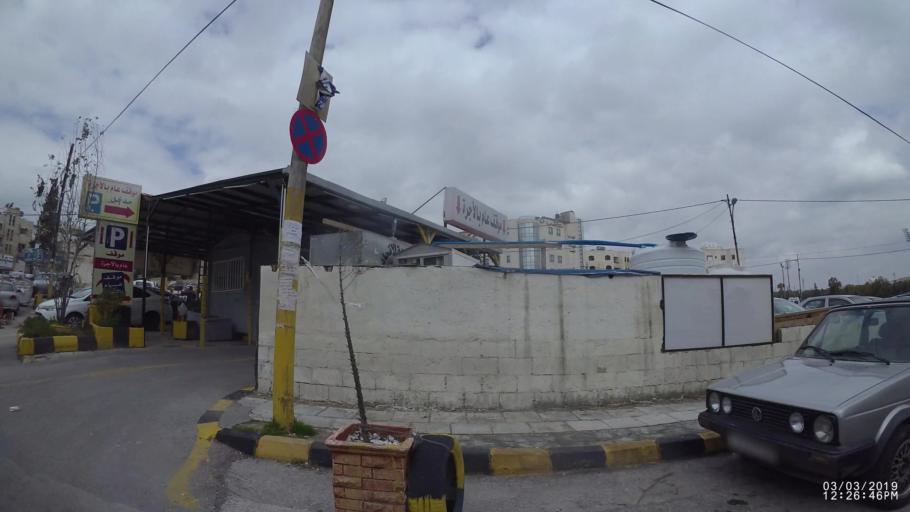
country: JO
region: Amman
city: Amman
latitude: 31.9792
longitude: 35.9004
